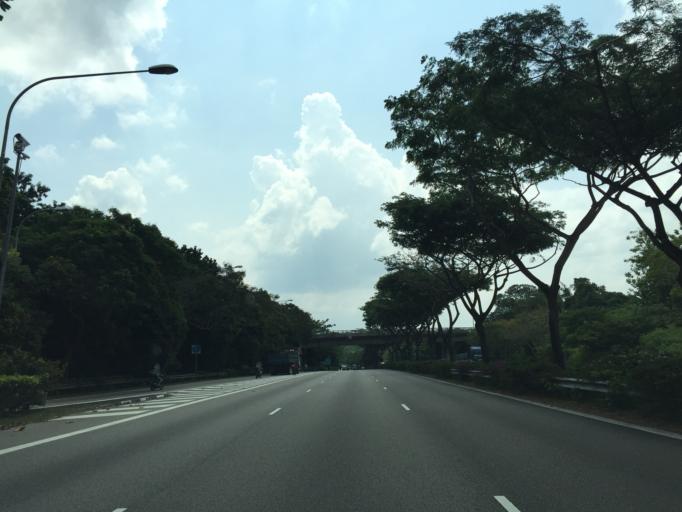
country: MY
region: Johor
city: Johor Bahru
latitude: 1.4198
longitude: 103.7712
